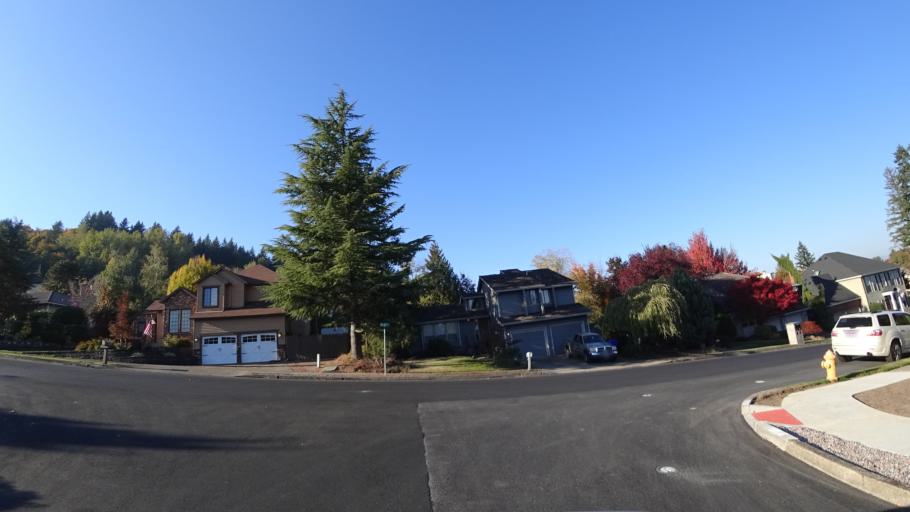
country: US
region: Oregon
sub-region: Multnomah County
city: Gresham
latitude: 45.4861
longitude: -122.4258
